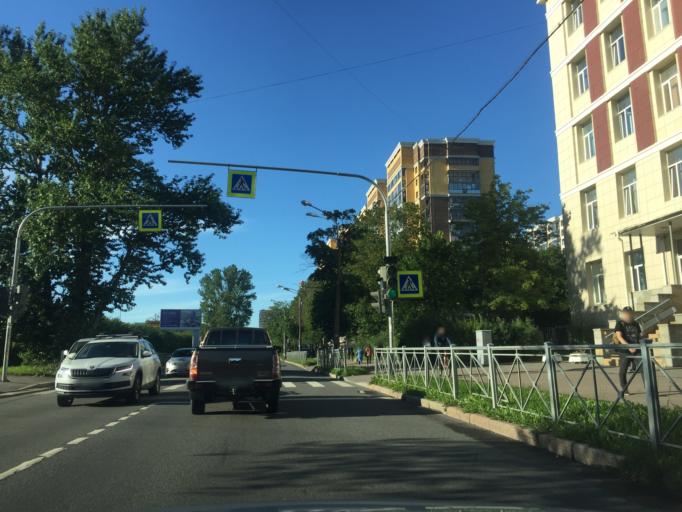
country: RU
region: St.-Petersburg
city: Admiralteisky
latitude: 59.8778
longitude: 30.3134
